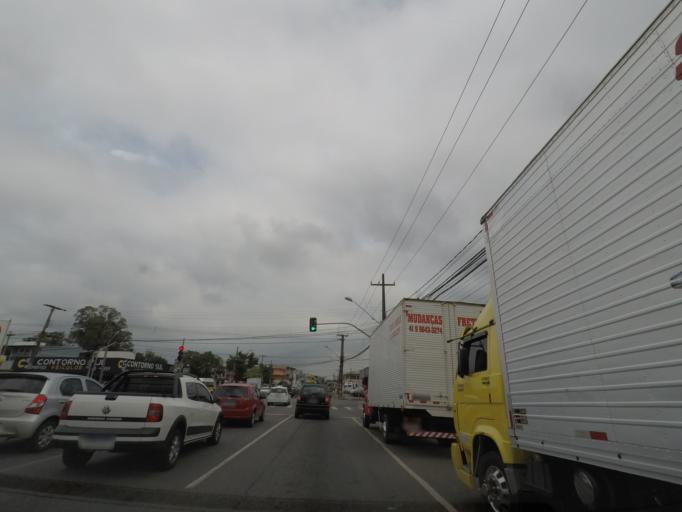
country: BR
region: Parana
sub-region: Curitiba
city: Curitiba
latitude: -25.5114
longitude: -49.3324
